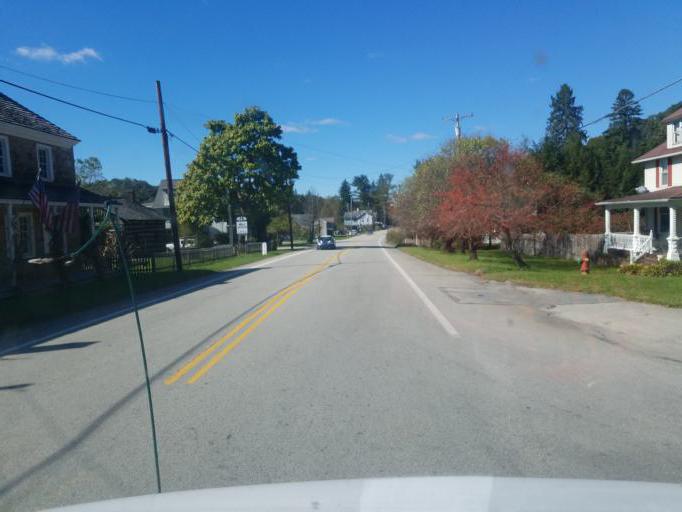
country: US
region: Pennsylvania
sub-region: Westmoreland County
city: Ligonier
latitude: 40.2120
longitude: -79.1986
